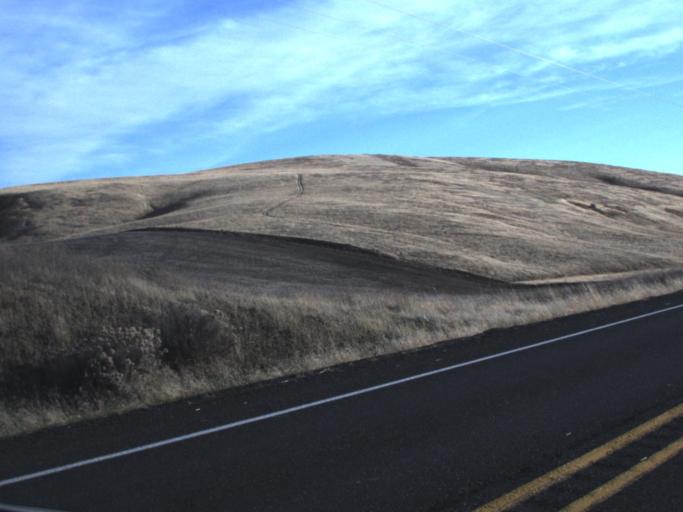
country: US
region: Washington
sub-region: Columbia County
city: Dayton
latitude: 46.4847
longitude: -117.9610
